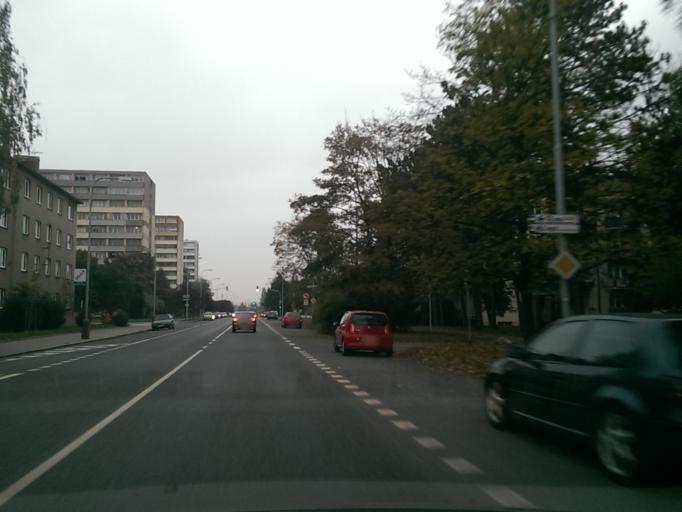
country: CZ
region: Central Bohemia
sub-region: Okres Mlada Boleslav
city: Mlada Boleslav
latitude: 50.4106
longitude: 14.9243
